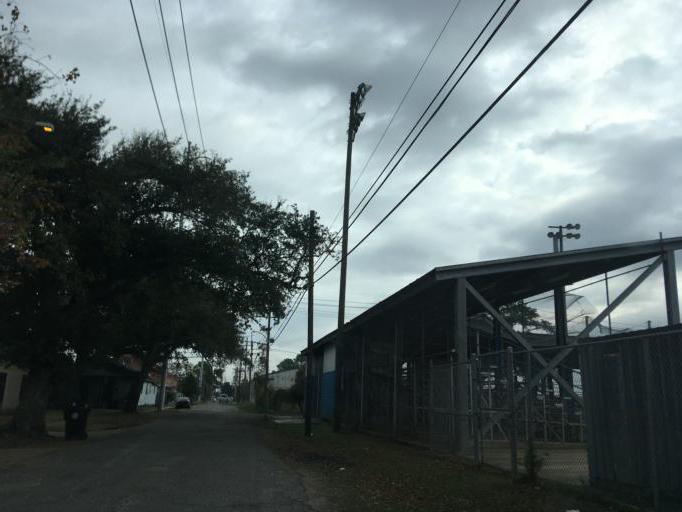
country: US
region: Louisiana
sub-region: Orleans Parish
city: New Orleans
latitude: 29.9886
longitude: -90.0615
